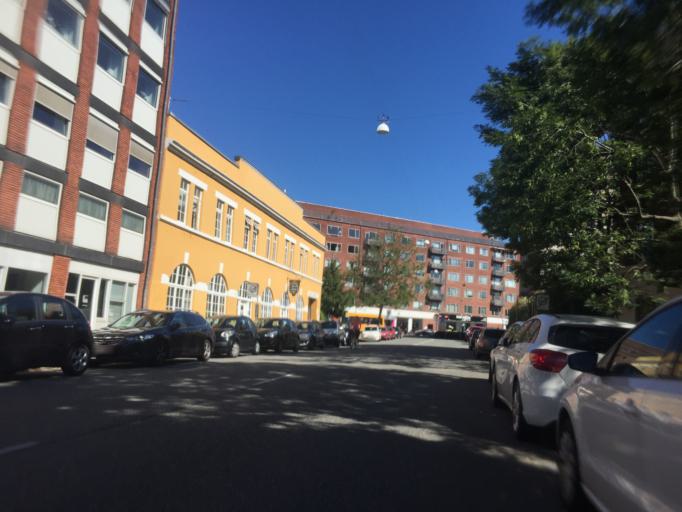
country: DK
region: Capital Region
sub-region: Kobenhavn
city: Copenhagen
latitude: 55.6810
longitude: 12.5561
